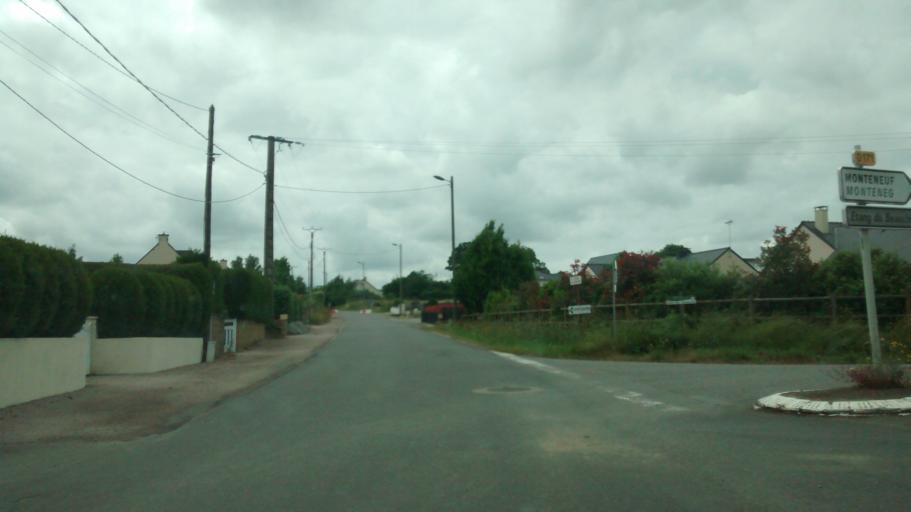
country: FR
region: Brittany
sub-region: Departement du Morbihan
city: Carentoir
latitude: 47.8182
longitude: -2.1419
